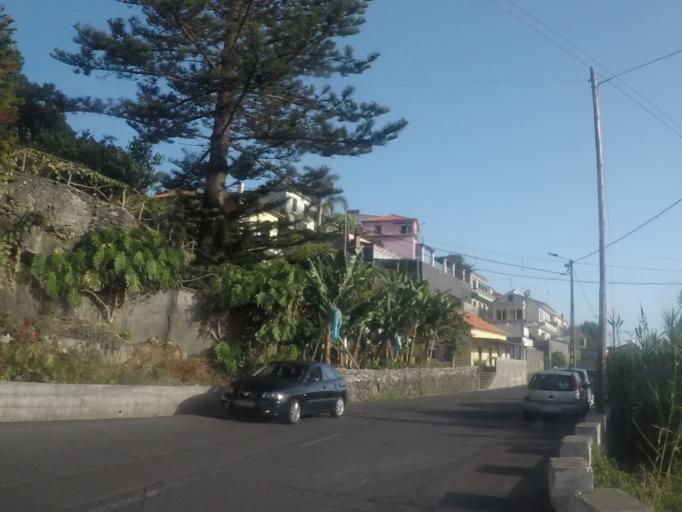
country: PT
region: Madeira
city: Ribeira Brava
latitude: 32.6771
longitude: -17.0667
